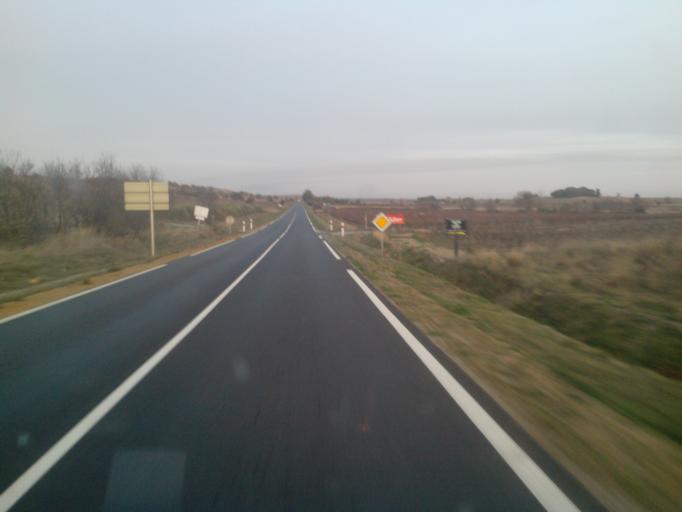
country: FR
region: Languedoc-Roussillon
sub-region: Departement de l'Aude
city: Ginestas
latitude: 43.2854
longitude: 2.8458
